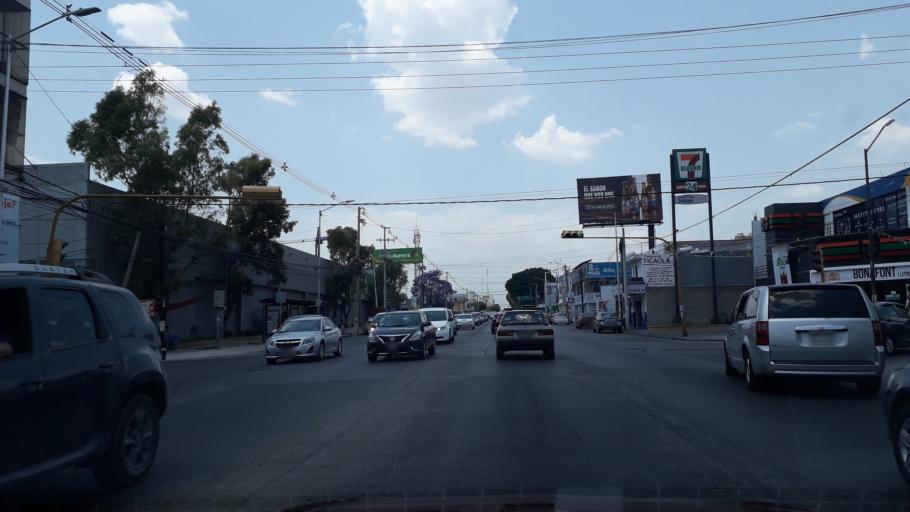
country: MX
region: Puebla
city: Puebla
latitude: 19.0357
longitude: -98.2113
